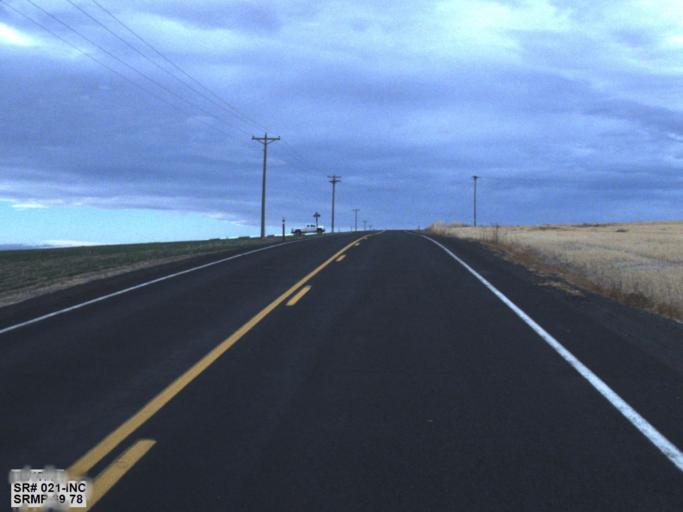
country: US
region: Washington
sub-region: Okanogan County
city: Coulee Dam
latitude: 47.4924
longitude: -118.7848
